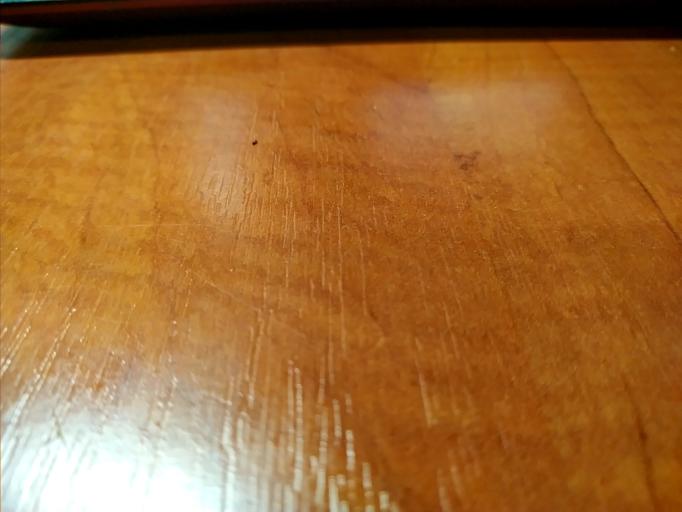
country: RU
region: Arkhangelskaya
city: Onega
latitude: 63.6306
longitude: 36.7788
